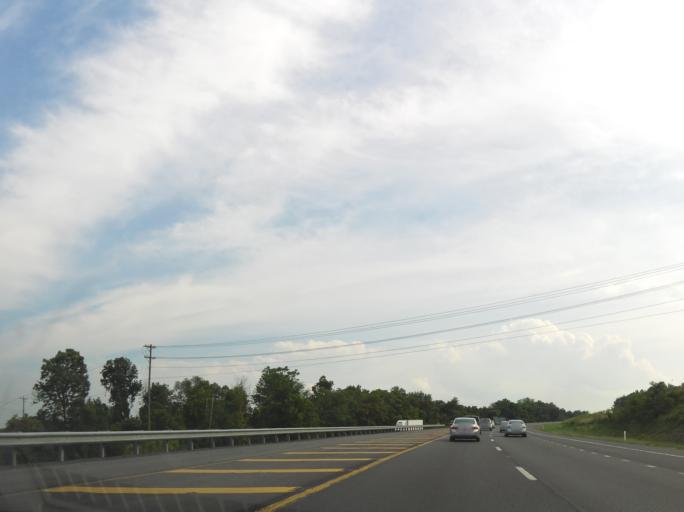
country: US
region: West Virginia
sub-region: Berkeley County
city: Martinsburg
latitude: 39.4397
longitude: -77.9895
